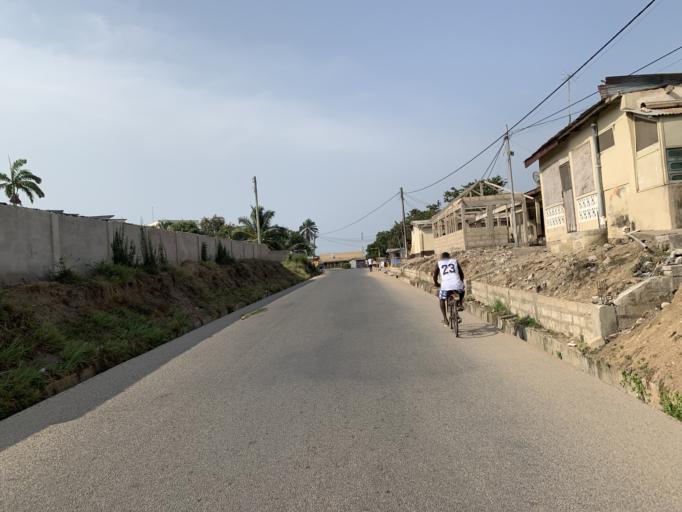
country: GH
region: Central
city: Winneba
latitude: 5.3363
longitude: -0.6251
